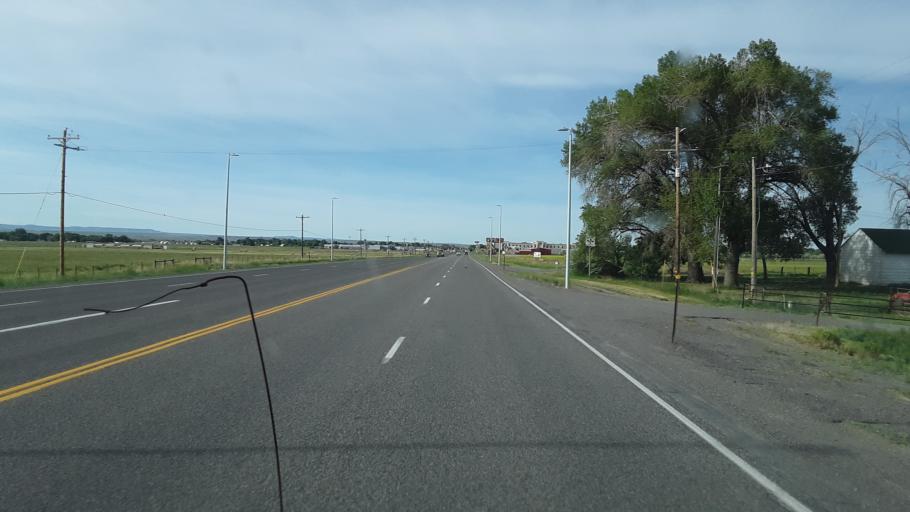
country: US
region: Wyoming
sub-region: Fremont County
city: Riverton
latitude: 43.0552
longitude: -108.3809
